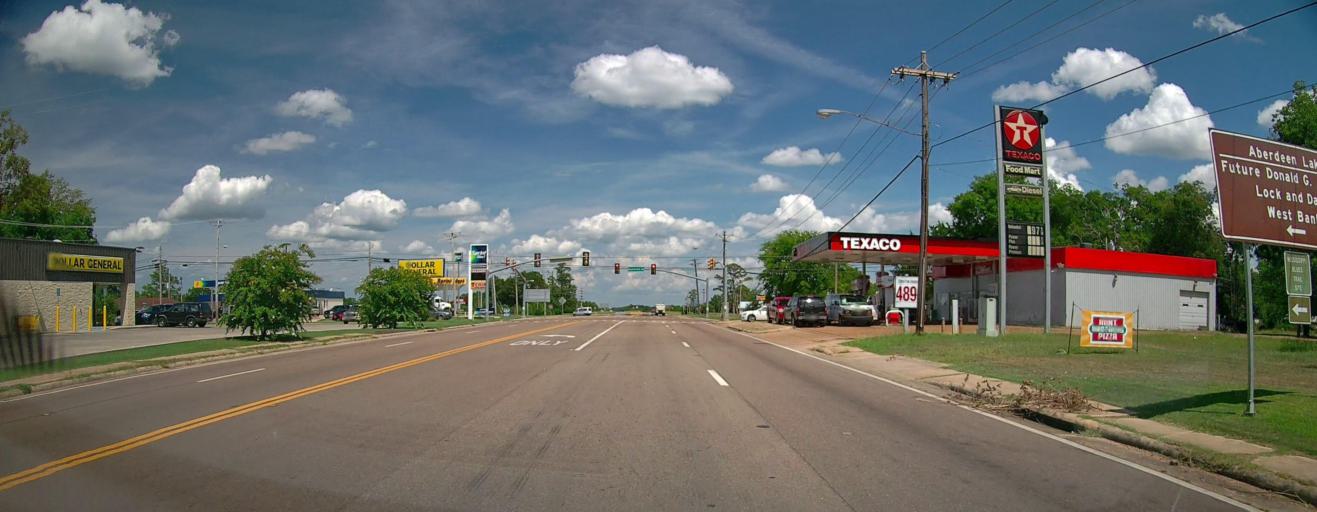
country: US
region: Mississippi
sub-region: Monroe County
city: Aberdeen
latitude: 33.8152
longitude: -88.5451
